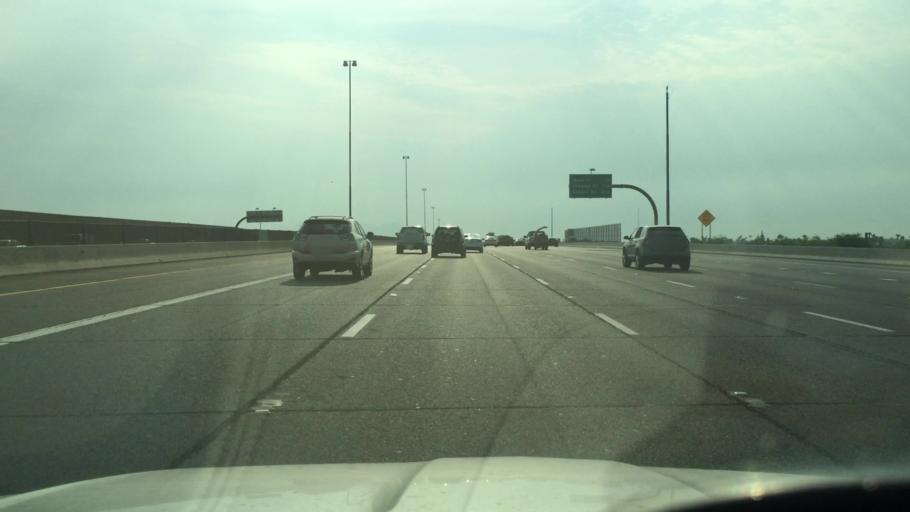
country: US
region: Arizona
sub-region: Maricopa County
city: Mesa
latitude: 33.3855
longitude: -111.8337
